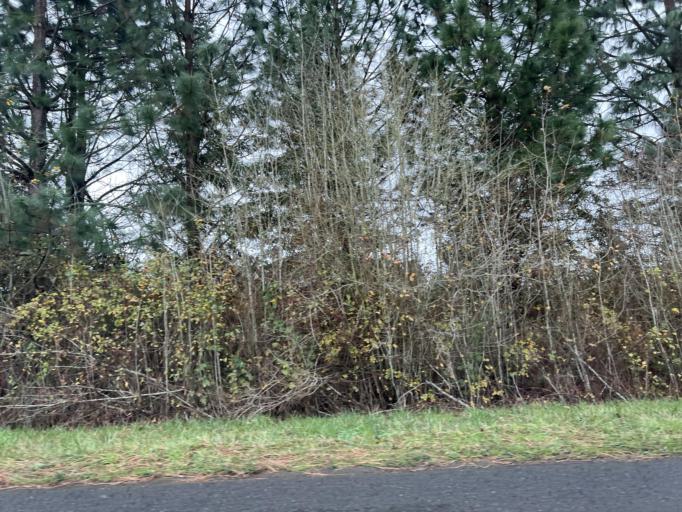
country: US
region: Oregon
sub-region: Polk County
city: Independence
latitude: 44.8095
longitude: -123.0853
